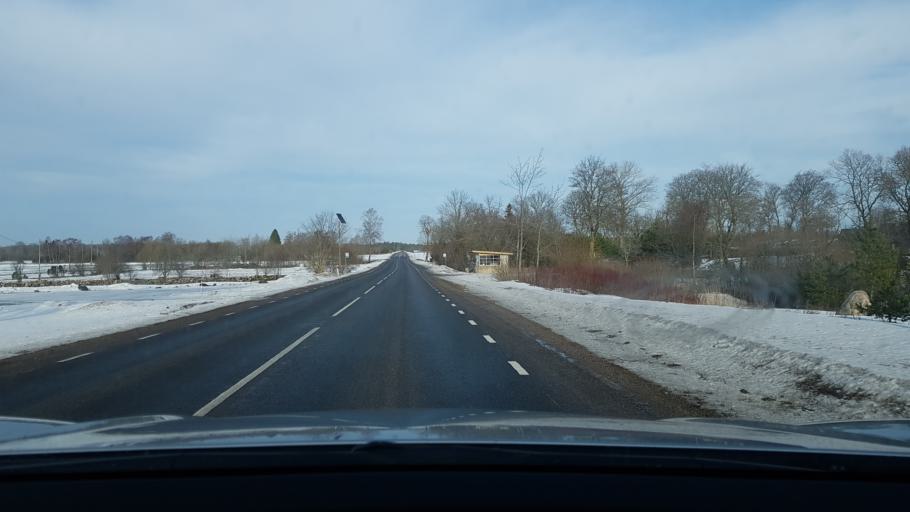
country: EE
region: Saare
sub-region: Kuressaare linn
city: Kuressaare
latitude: 58.3068
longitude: 22.5404
